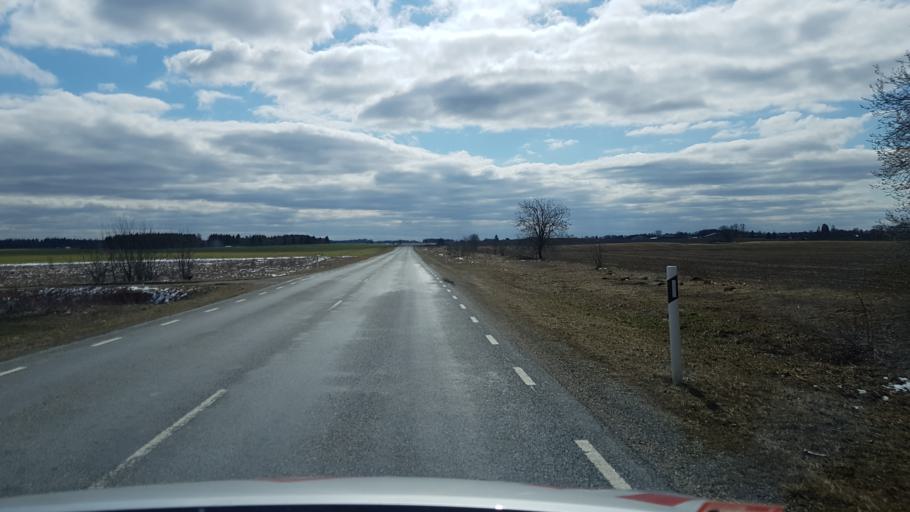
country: EE
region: Laeaene-Virumaa
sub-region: Tapa vald
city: Tapa
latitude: 59.3209
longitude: 26.0040
